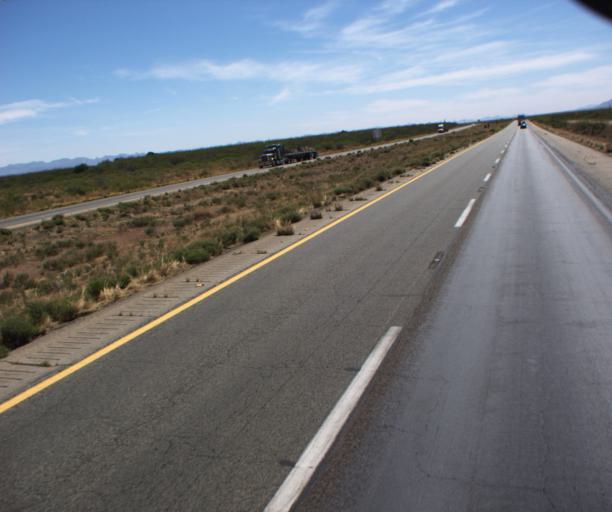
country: US
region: Arizona
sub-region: Cochise County
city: Willcox
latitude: 32.3251
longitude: -109.5064
